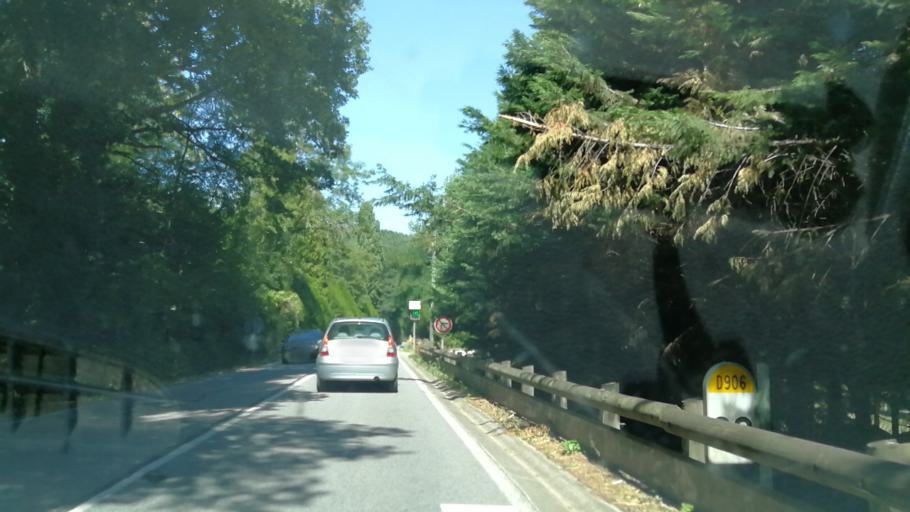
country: FR
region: Ile-de-France
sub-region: Departement des Yvelines
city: Chevreuse
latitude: 48.6871
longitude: 2.0139
